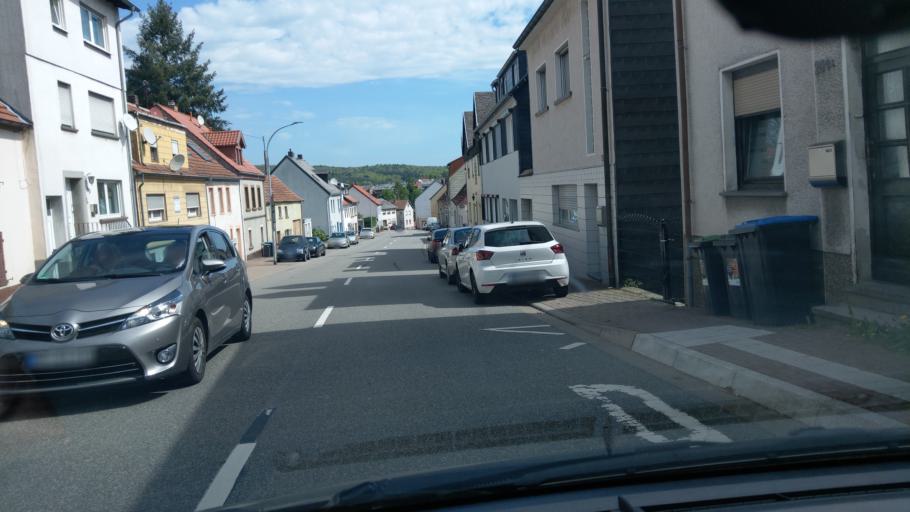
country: DE
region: Saarland
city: Spiesen-Elversberg
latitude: 49.3122
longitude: 7.1476
